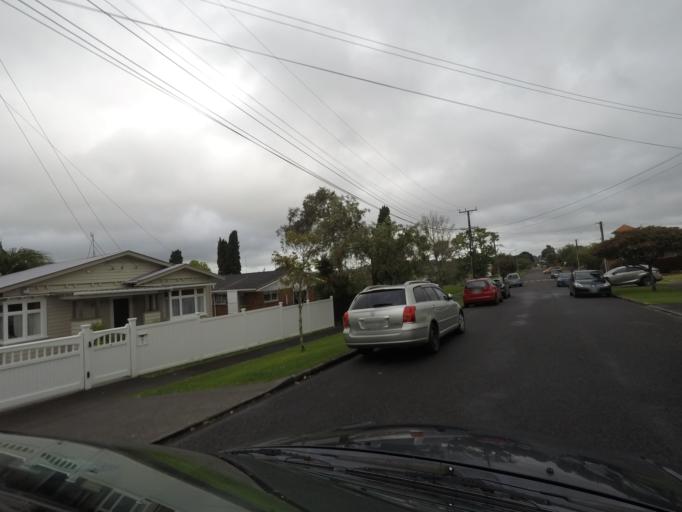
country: NZ
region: Auckland
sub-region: Auckland
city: Auckland
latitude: -36.8946
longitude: 174.7311
